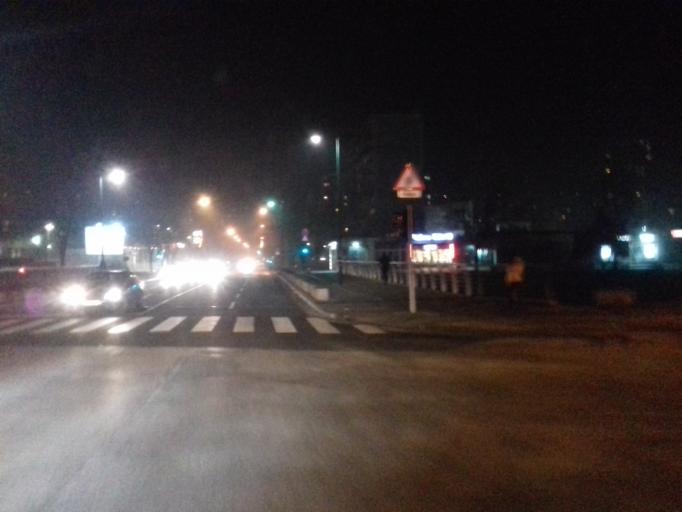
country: BA
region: Federation of Bosnia and Herzegovina
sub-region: Kanton Sarajevo
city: Sarajevo
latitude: 43.8517
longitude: 18.3855
